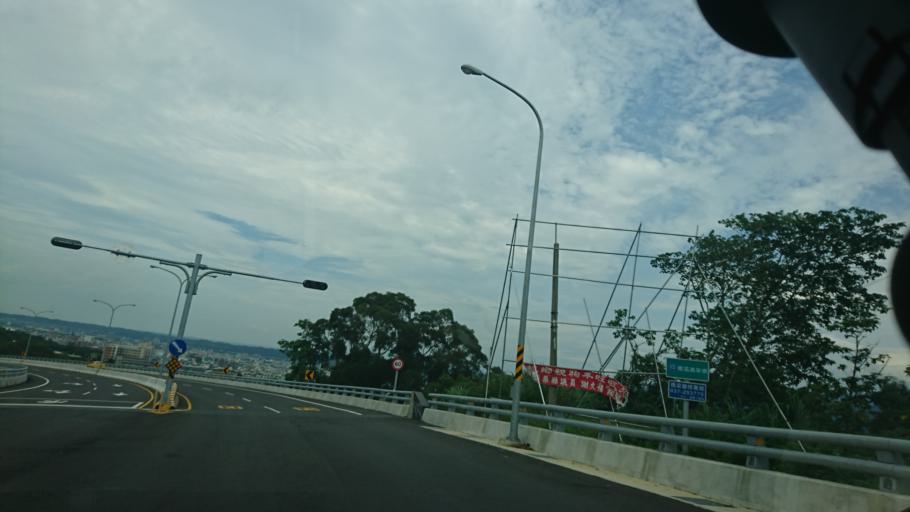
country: TW
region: Taiwan
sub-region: Miaoli
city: Miaoli
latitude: 24.5365
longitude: 120.8089
